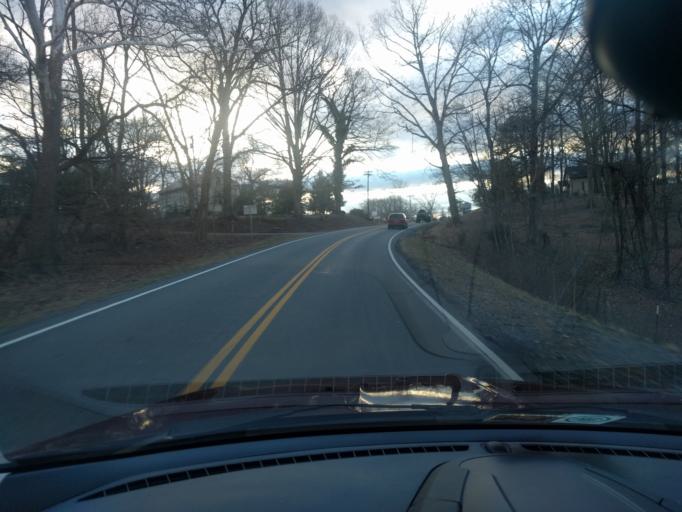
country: US
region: Virginia
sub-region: City of Bedford
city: Bedford
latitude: 37.3800
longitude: -79.5503
